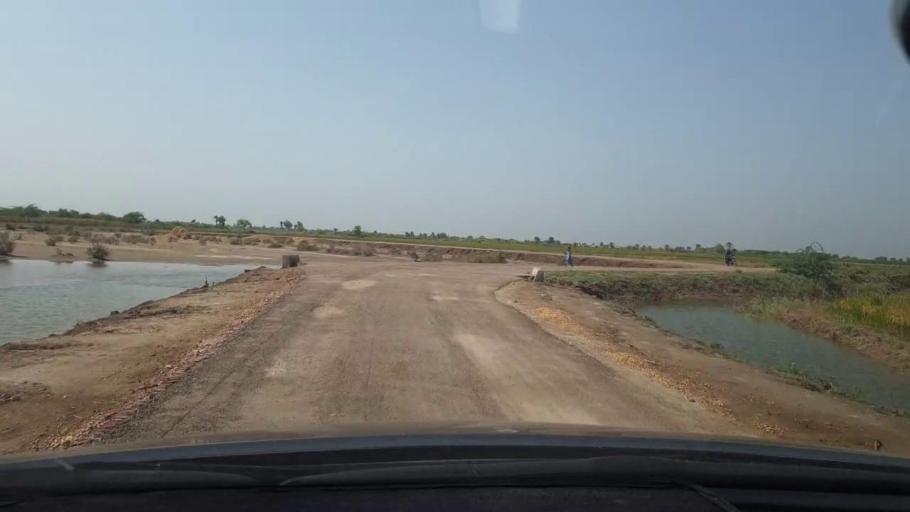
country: PK
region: Sindh
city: Tando Bago
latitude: 24.7000
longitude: 69.1069
